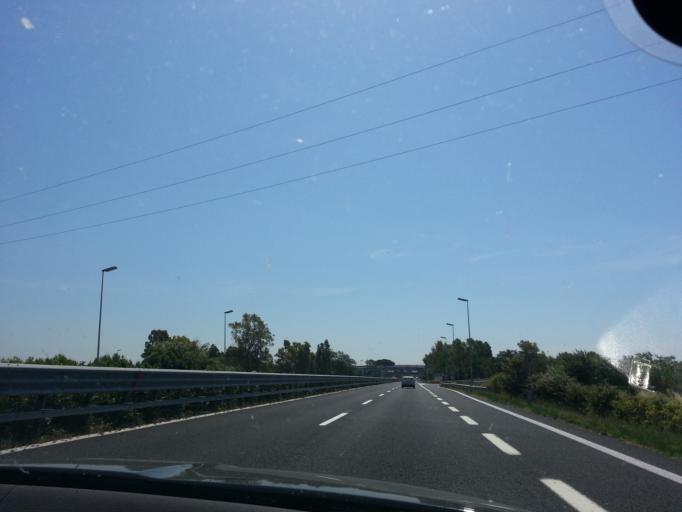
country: IT
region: Latium
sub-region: Citta metropolitana di Roma Capitale
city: Cerveteri
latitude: 41.9825
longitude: 12.0781
